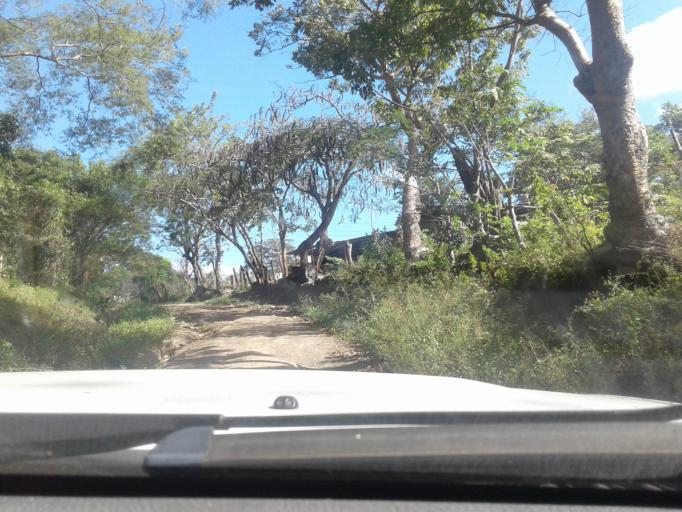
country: NI
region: Carazo
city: Santa Teresa
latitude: 11.7583
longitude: -86.1793
